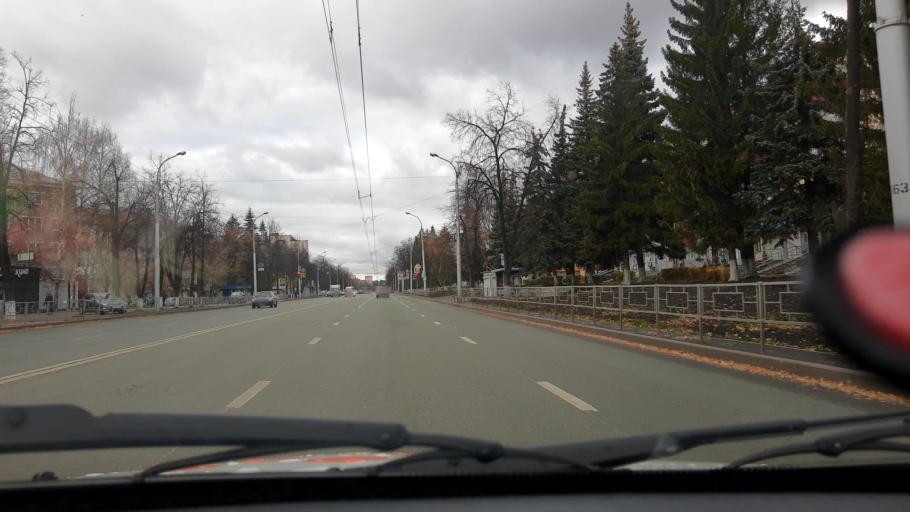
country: RU
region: Bashkortostan
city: Ufa
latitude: 54.8082
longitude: 56.1078
